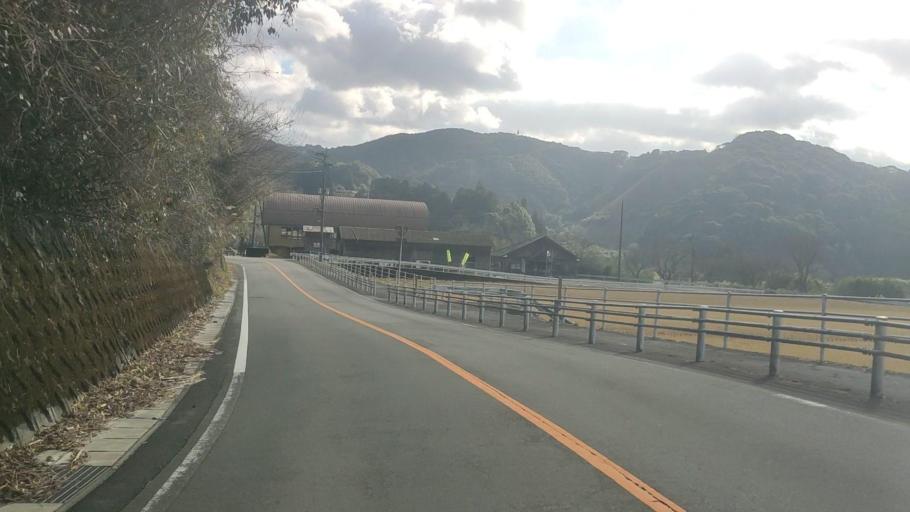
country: JP
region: Kumamoto
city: Hitoyoshi
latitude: 32.2913
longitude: 130.8425
